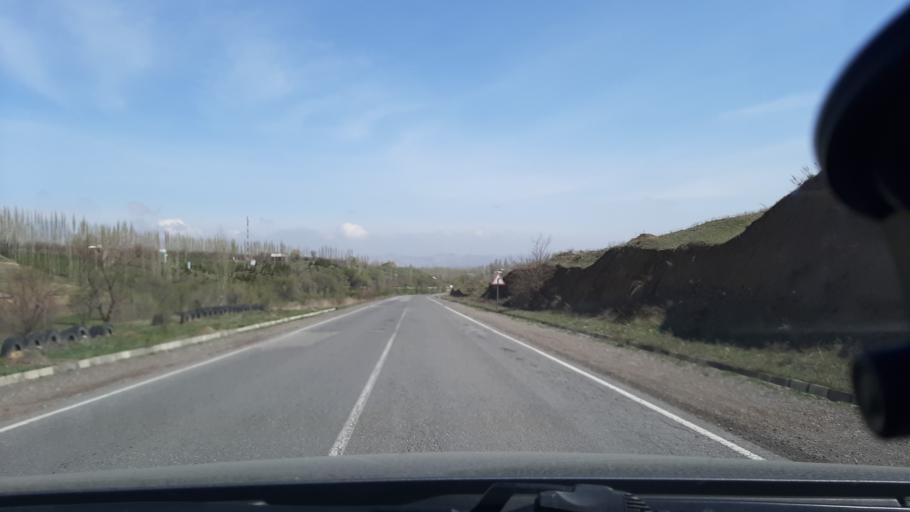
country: TJ
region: Viloyati Sughd
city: Shahriston
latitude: 39.7757
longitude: 68.8289
